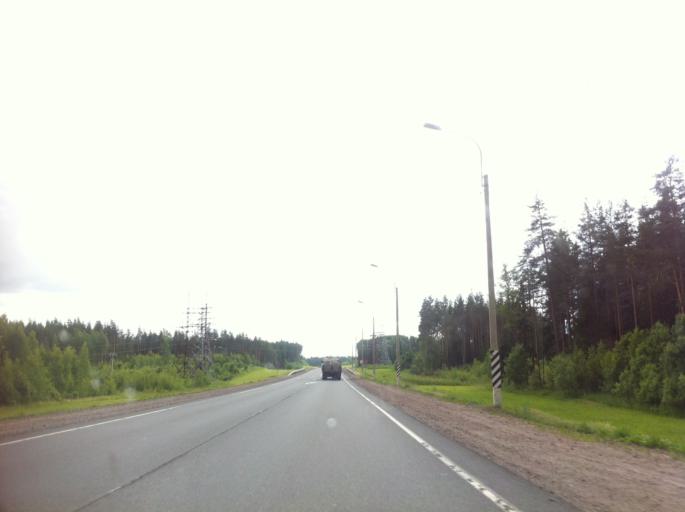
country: RU
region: Leningrad
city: Luga
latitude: 58.7750
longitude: 29.8802
